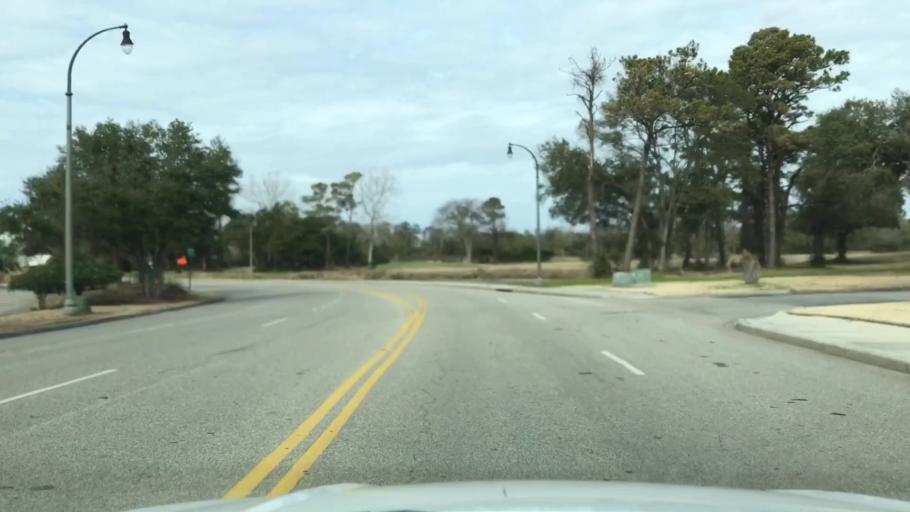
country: US
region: South Carolina
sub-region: Horry County
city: North Myrtle Beach
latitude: 33.8000
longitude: -78.7369
